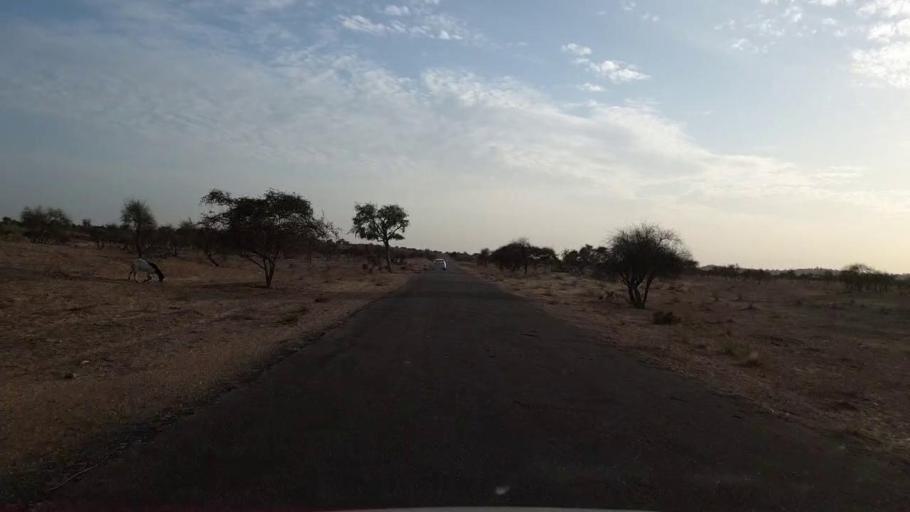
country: PK
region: Sindh
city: Nabisar
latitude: 25.0667
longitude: 69.9687
